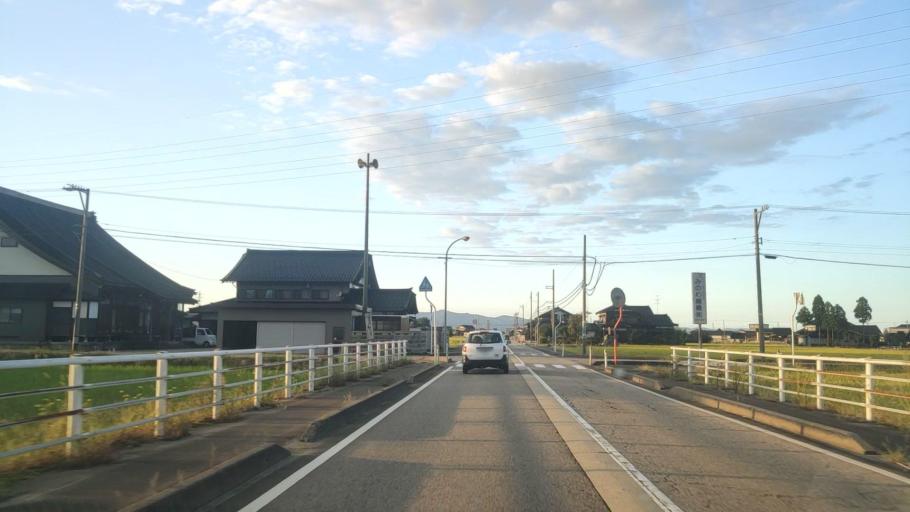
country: JP
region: Toyama
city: Nanto-shi
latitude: 36.6200
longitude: 136.8890
